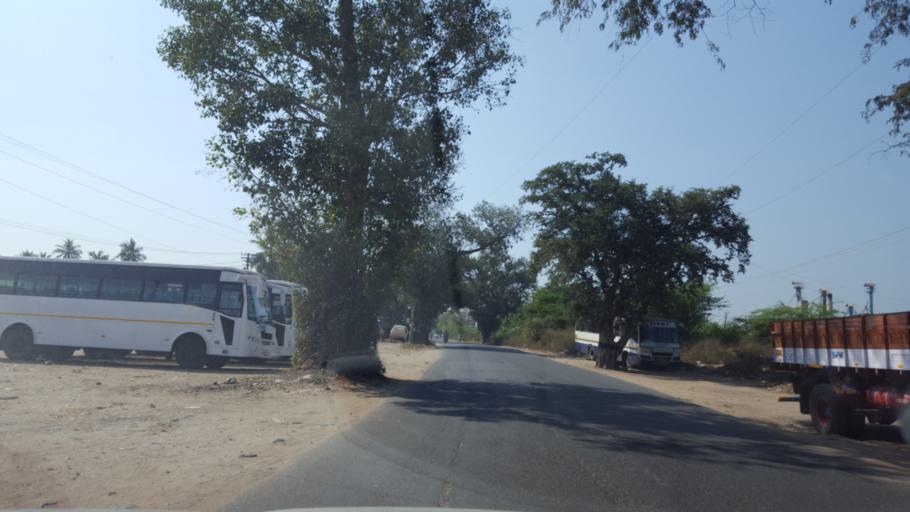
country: IN
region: Tamil Nadu
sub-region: Kancheepuram
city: Kanchipuram
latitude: 12.8569
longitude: 79.6828
